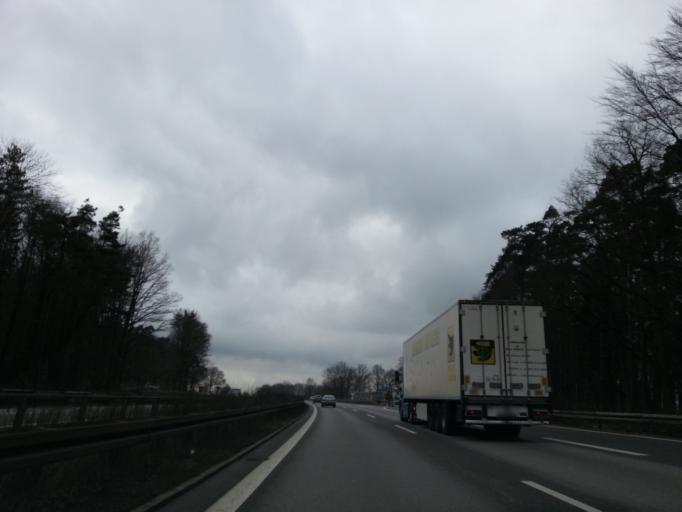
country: DE
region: Bavaria
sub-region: Upper Palatinate
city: Sinzing
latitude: 49.0080
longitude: 11.9963
